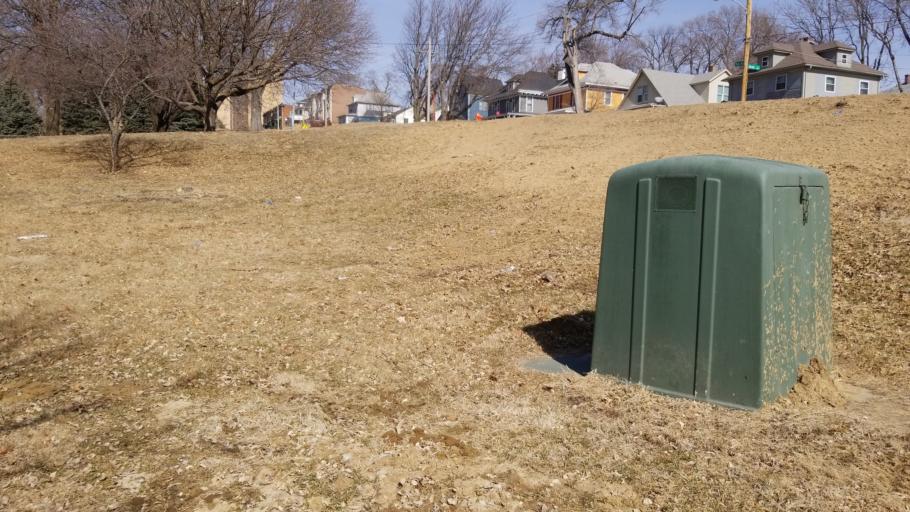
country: US
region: Nebraska
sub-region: Douglas County
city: Omaha
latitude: 41.2409
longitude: -95.9560
